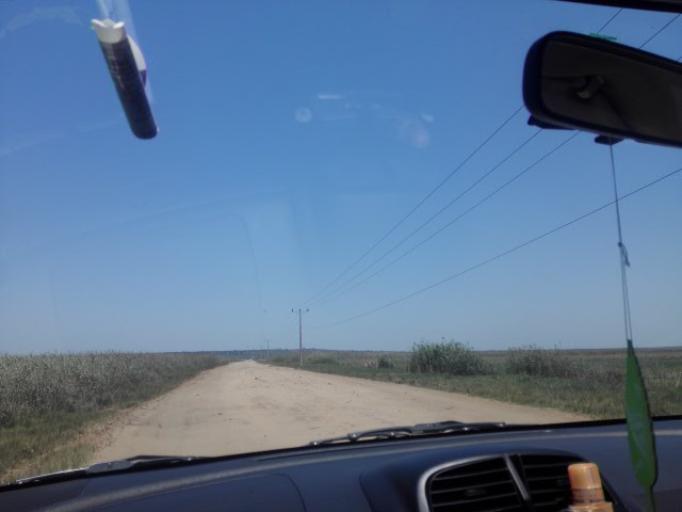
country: MZ
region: Maputo City
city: Maputo
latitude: -25.7313
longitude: 32.7173
